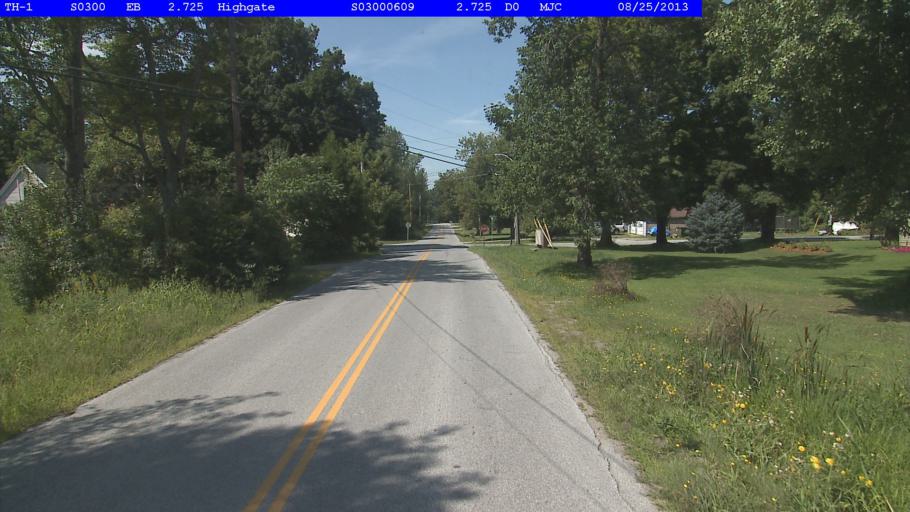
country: US
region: Vermont
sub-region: Franklin County
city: Swanton
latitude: 44.9623
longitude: -73.0957
